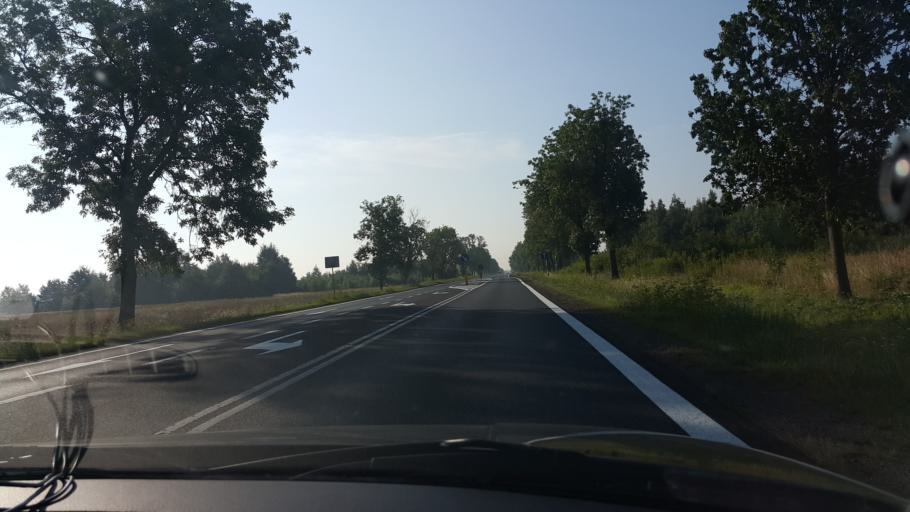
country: PL
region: Masovian Voivodeship
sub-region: Powiat radomski
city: Jedlnia-Letnisko
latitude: 51.3983
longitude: 21.2598
